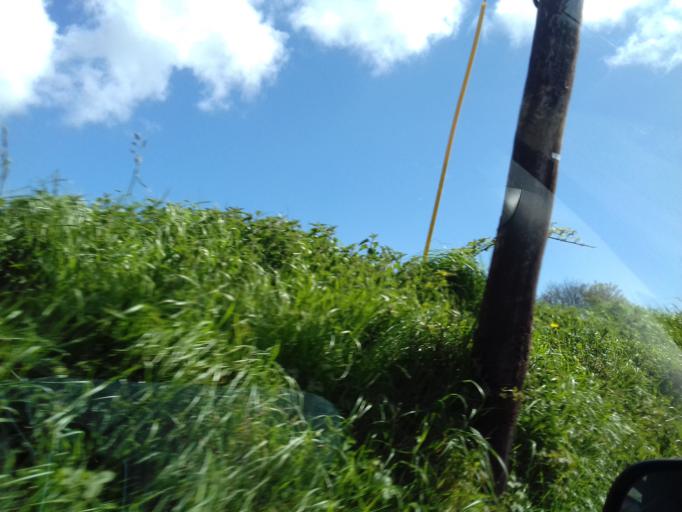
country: IE
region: Leinster
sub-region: Loch Garman
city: Castlebridge
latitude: 52.3911
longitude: -6.3849
